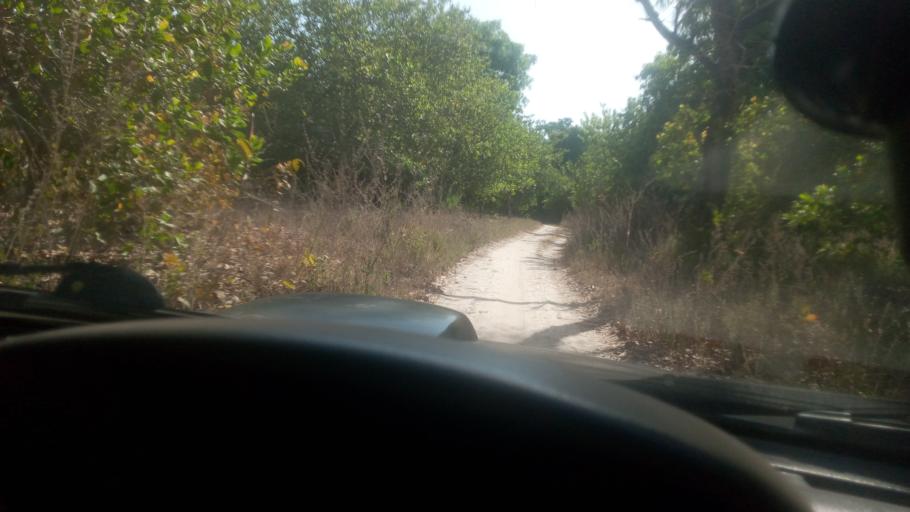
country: GW
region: Oio
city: Farim
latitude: 12.4465
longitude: -15.4335
